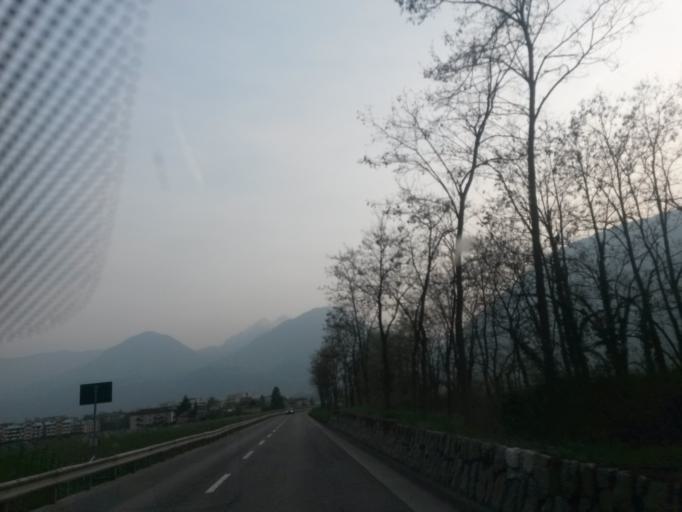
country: IT
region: Trentino-Alto Adige
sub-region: Bolzano
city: Sinigo
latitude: 46.6517
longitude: 11.1815
